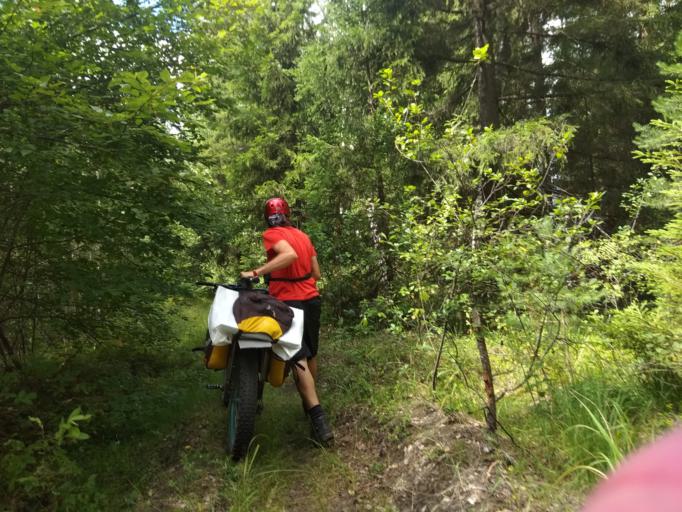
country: RU
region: Moskovskaya
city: Misheronskiy
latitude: 55.6459
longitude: 39.6946
